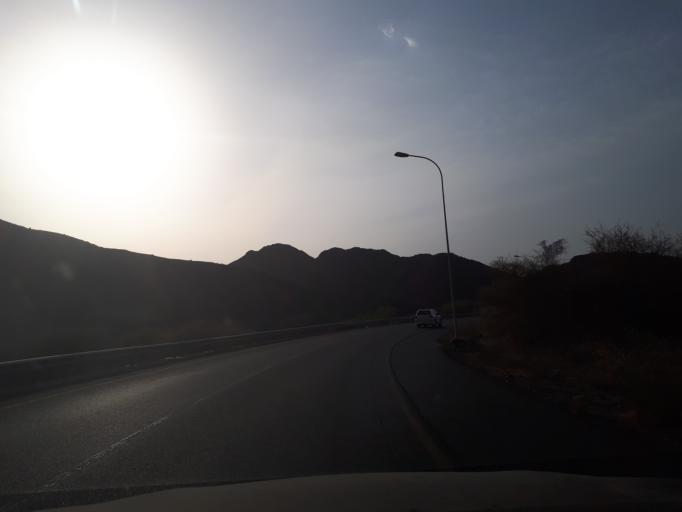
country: OM
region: Muhafazat ad Dakhiliyah
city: Sufalat Sama'il
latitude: 23.1716
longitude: 58.0964
